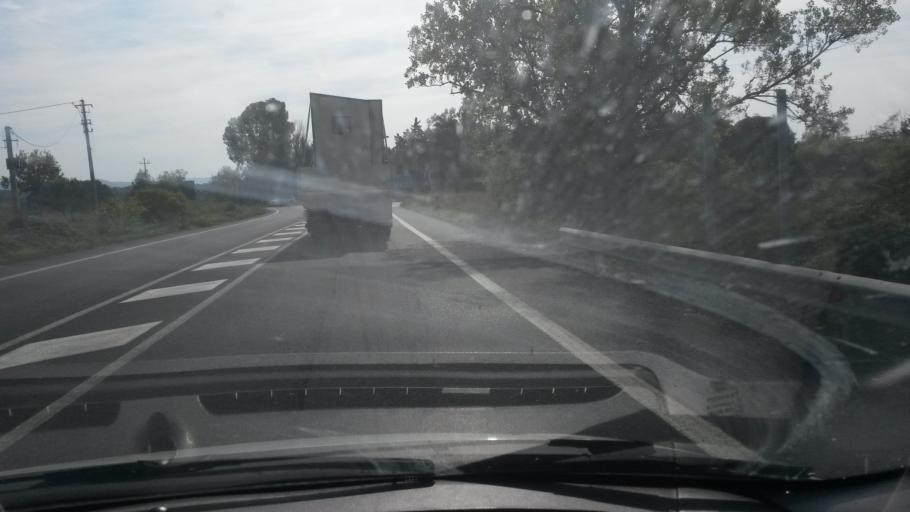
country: IT
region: Tuscany
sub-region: Provincia di Livorno
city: S.P. in Palazzi
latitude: 43.3333
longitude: 10.5267
